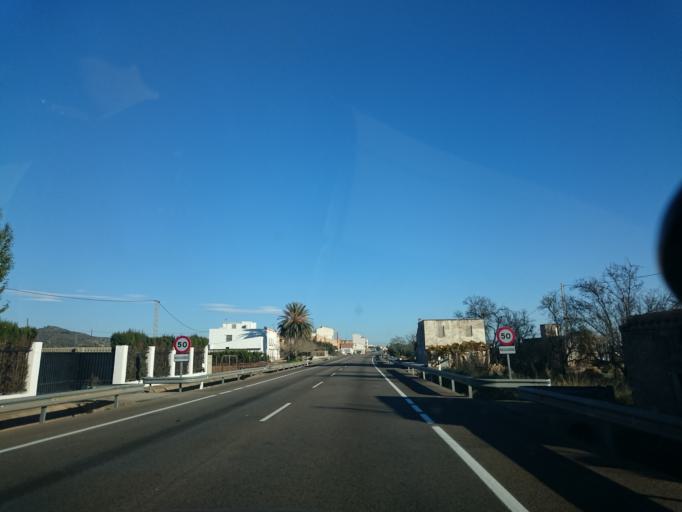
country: ES
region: Valencia
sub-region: Provincia de Castello
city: Orpesa/Oropesa del Mar
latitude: 40.1494
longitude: 0.1566
